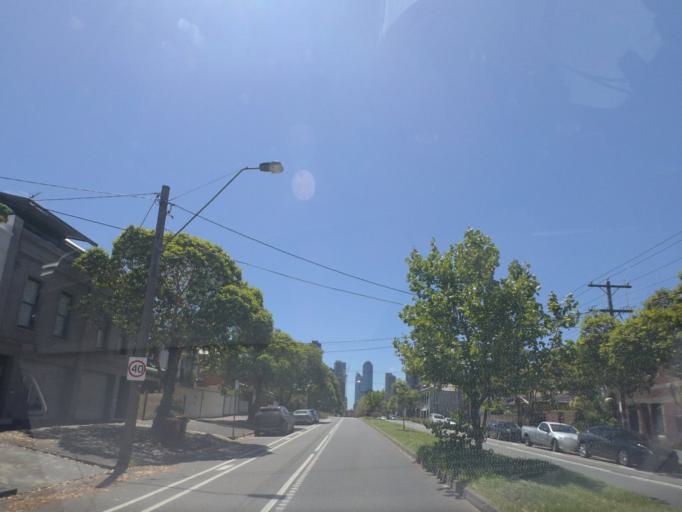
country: AU
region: Victoria
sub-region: Port Phillip
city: South Melbourne
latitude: -37.8341
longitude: 144.9639
